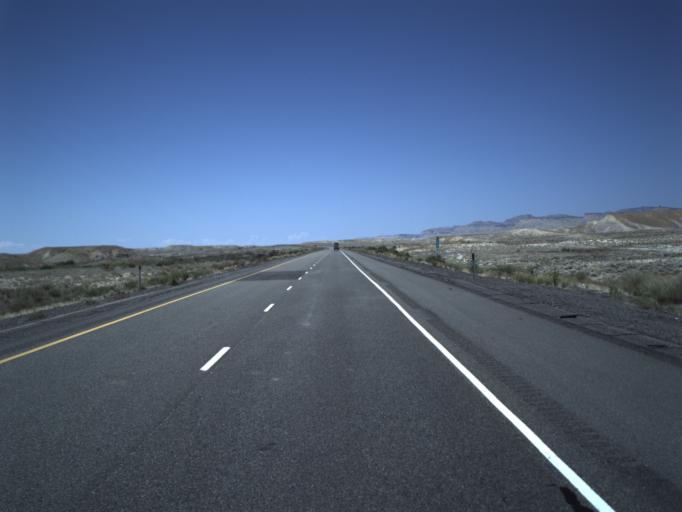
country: US
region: Utah
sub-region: Grand County
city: Moab
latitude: 38.9409
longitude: -109.5107
